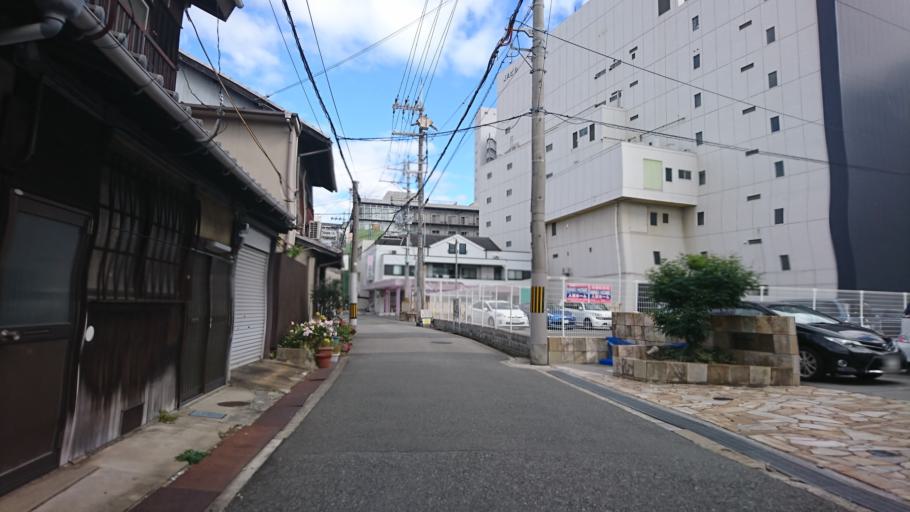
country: JP
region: Hyogo
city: Kakogawacho-honmachi
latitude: 34.7658
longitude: 134.8358
